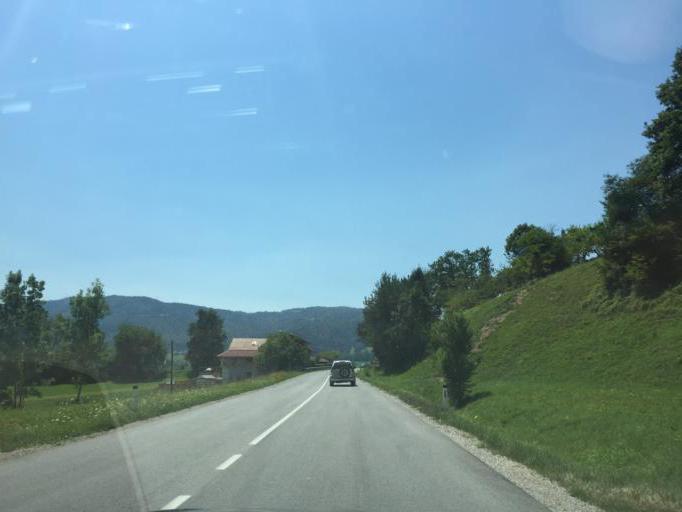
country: SI
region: Gorenja Vas-Poljane
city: Gorenja Vas
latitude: 46.1122
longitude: 14.1582
